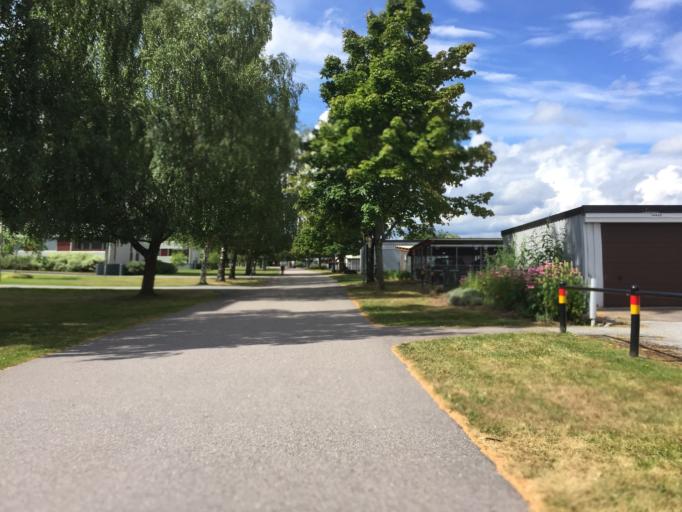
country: SE
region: OErebro
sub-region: Orebro Kommun
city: Orebro
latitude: 59.2743
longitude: 15.1720
